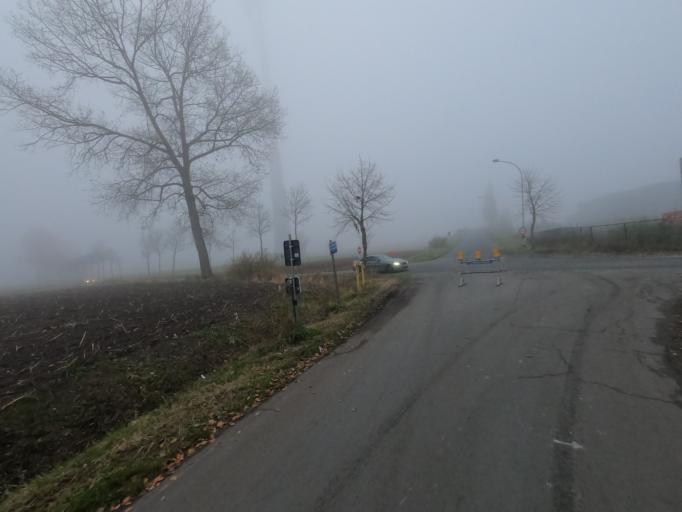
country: BE
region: Flanders
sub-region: Provincie Oost-Vlaanderen
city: Kruibeke
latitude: 51.1920
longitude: 4.3106
